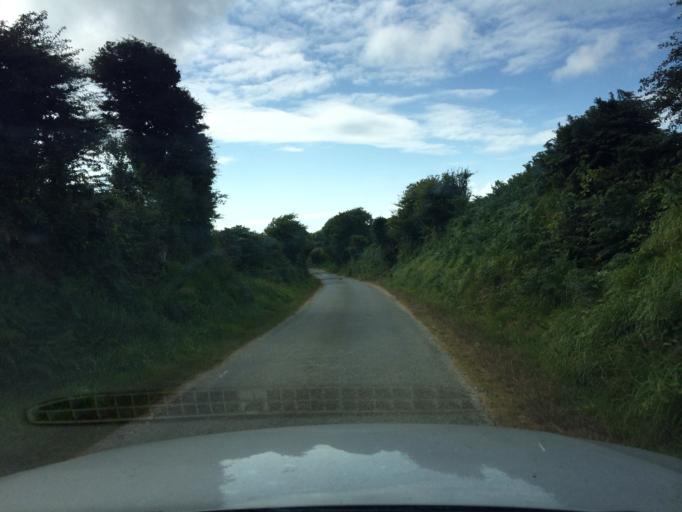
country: FR
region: Lower Normandy
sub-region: Departement de la Manche
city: Beaumont-Hague
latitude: 49.6873
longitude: -1.8816
